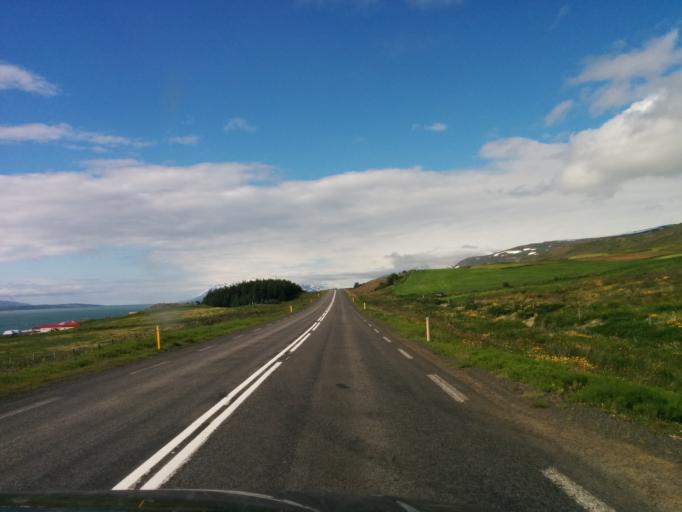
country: IS
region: Northeast
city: Akureyri
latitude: 65.7284
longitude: -18.0736
